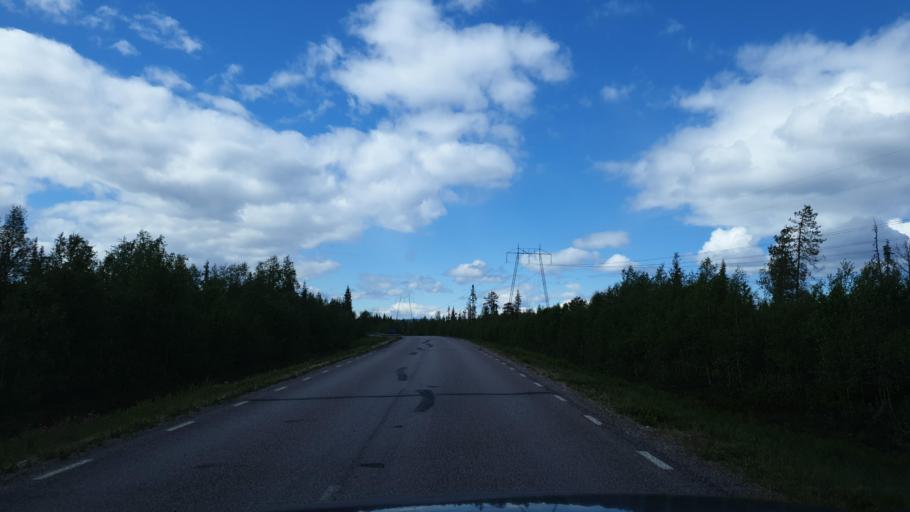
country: SE
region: Norrbotten
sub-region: Jokkmokks Kommun
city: Jokkmokk
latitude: 67.0993
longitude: 19.7438
